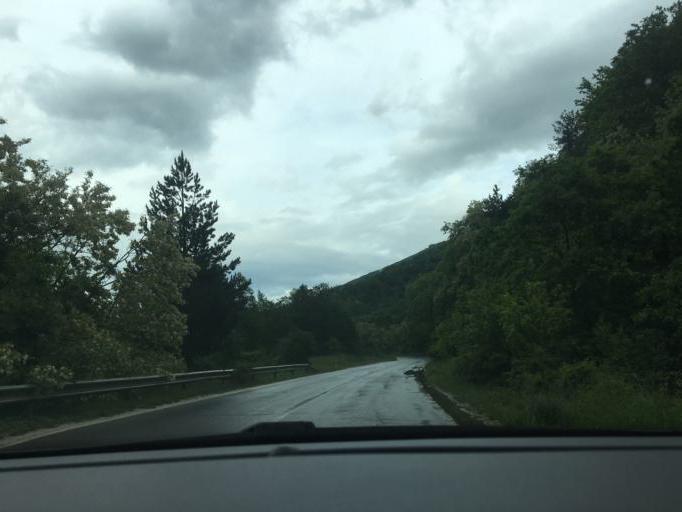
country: MK
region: Debarca
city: Meseista
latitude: 41.2648
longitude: 20.7774
